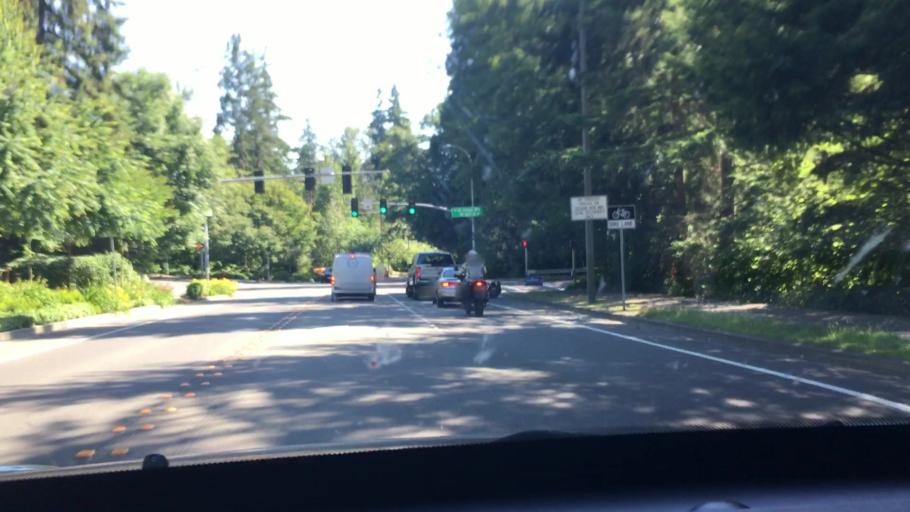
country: US
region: Washington
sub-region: King County
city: Newcastle
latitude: 47.5470
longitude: -122.1292
